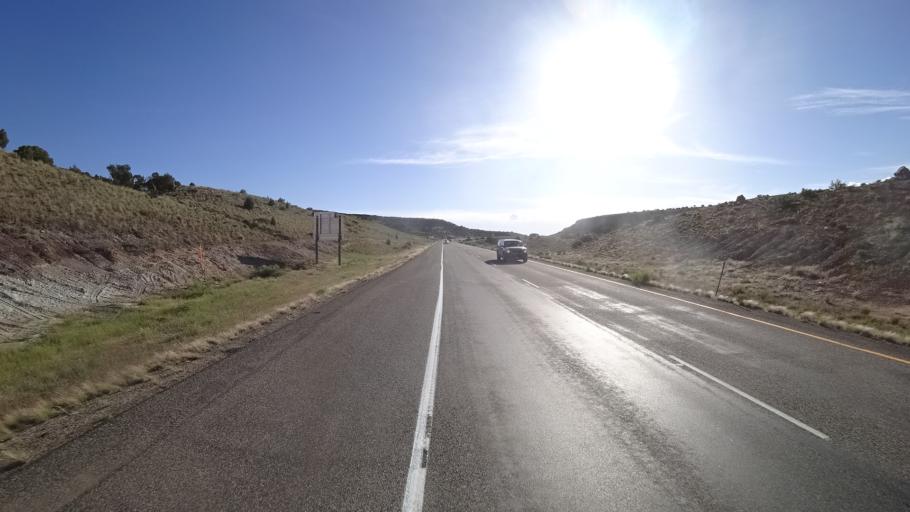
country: US
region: Colorado
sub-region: Mesa County
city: Loma
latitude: 39.1890
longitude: -109.0261
